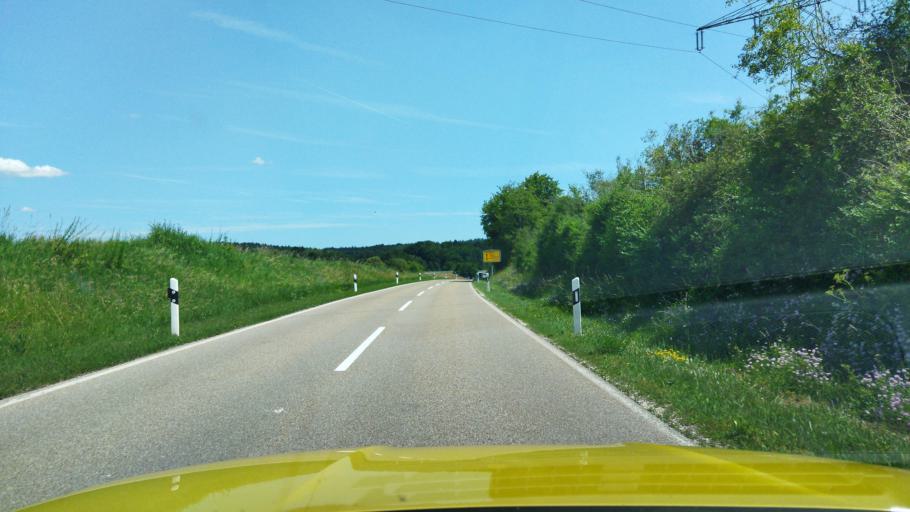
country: DE
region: Bavaria
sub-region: Lower Bavaria
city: Riedenburg
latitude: 48.9525
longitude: 11.6197
